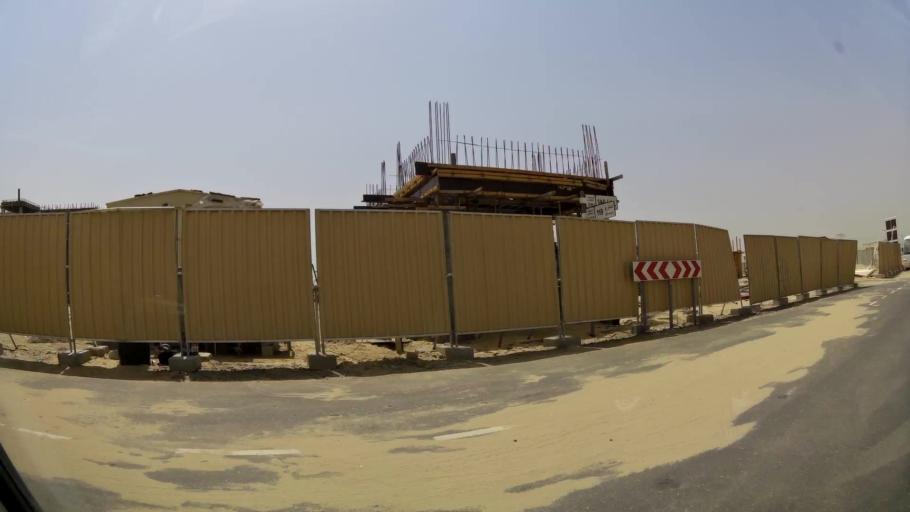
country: AE
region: Ash Shariqah
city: Sharjah
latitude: 25.2534
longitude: 55.4954
